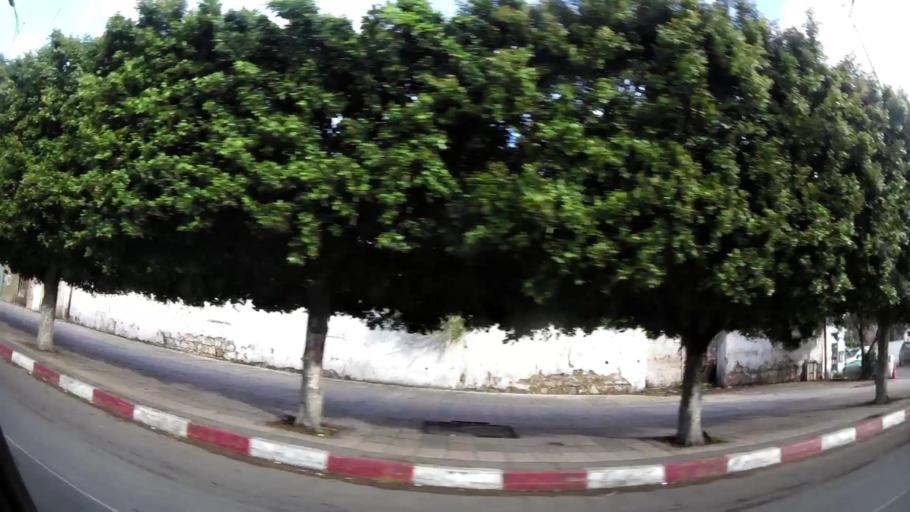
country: MA
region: Grand Casablanca
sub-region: Mohammedia
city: Mohammedia
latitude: 33.6935
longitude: -7.3918
